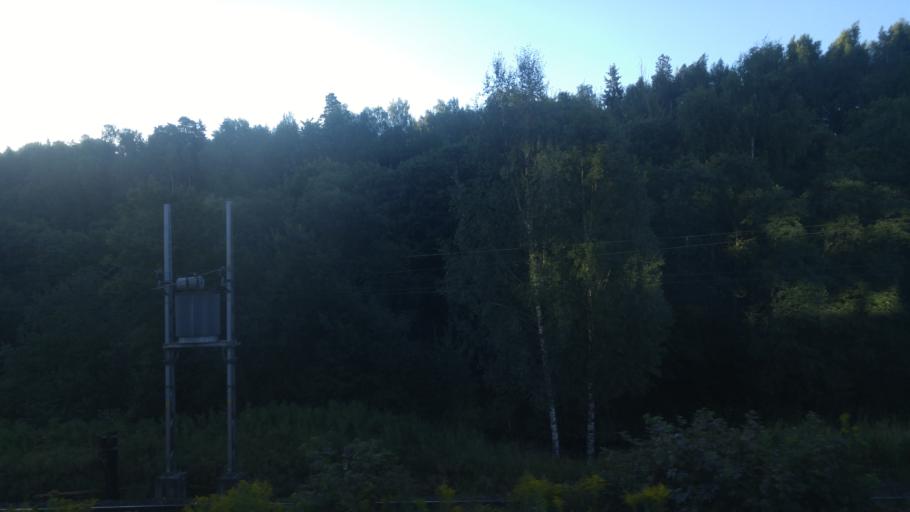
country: NO
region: Oslo
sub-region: Oslo
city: Oslo
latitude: 59.9133
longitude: 10.8273
